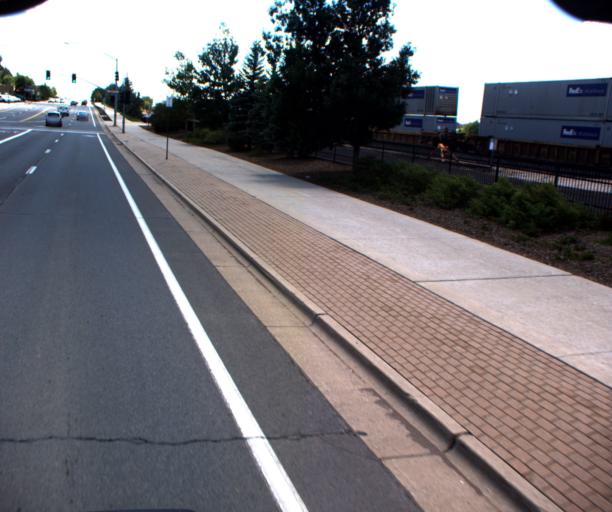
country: US
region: Arizona
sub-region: Coconino County
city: Flagstaff
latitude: 35.1967
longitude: -111.6467
